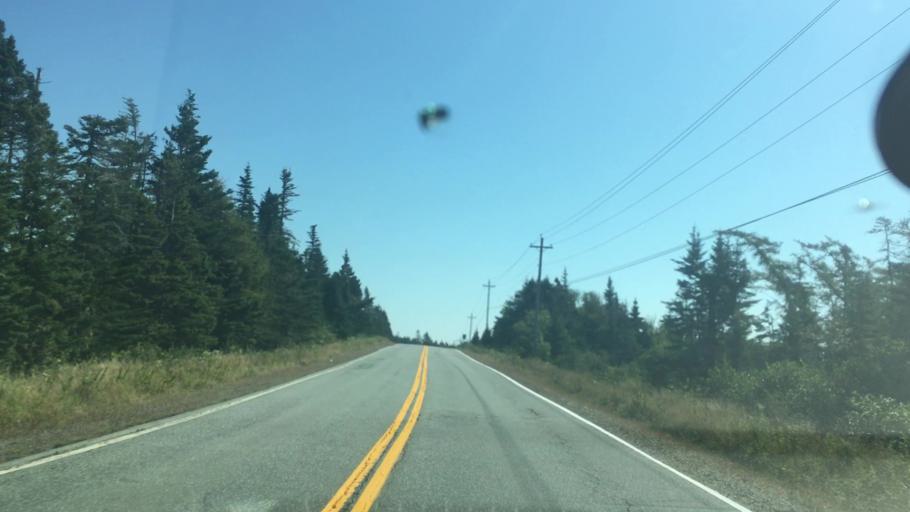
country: CA
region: Nova Scotia
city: New Glasgow
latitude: 44.9179
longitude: -62.3318
